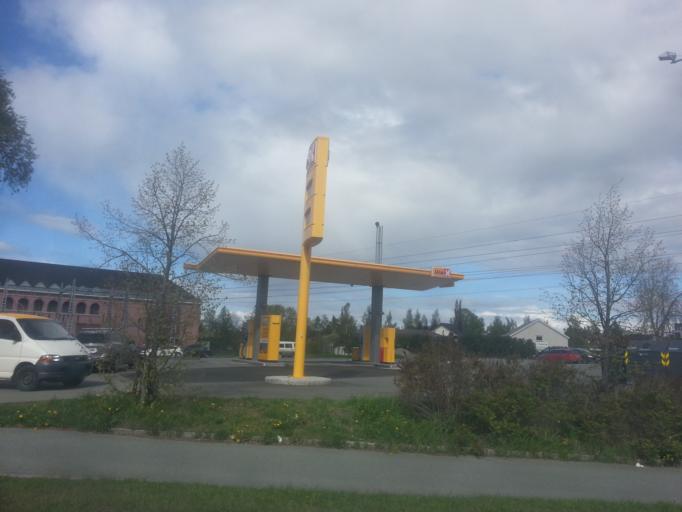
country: NO
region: Sor-Trondelag
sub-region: Trondheim
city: Trondheim
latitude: 63.4103
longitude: 10.4361
